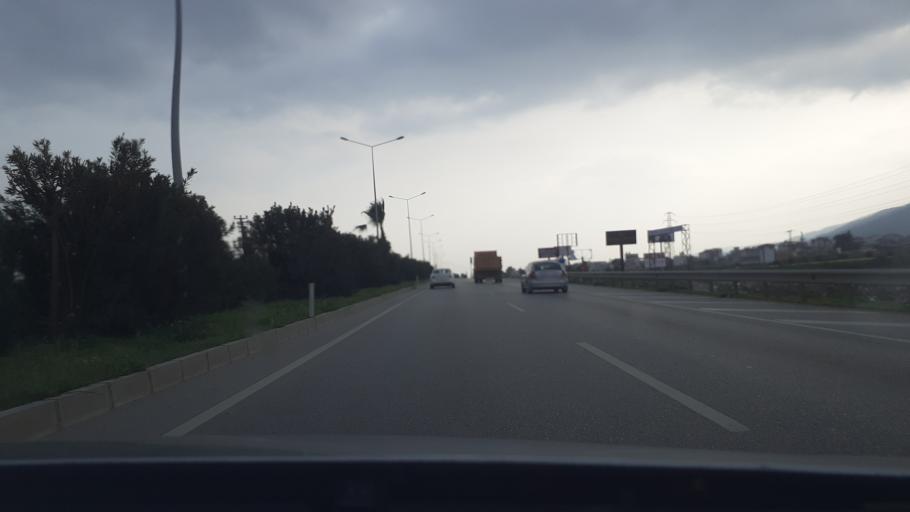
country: TR
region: Hatay
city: Serinyol
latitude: 36.3686
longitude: 36.2244
